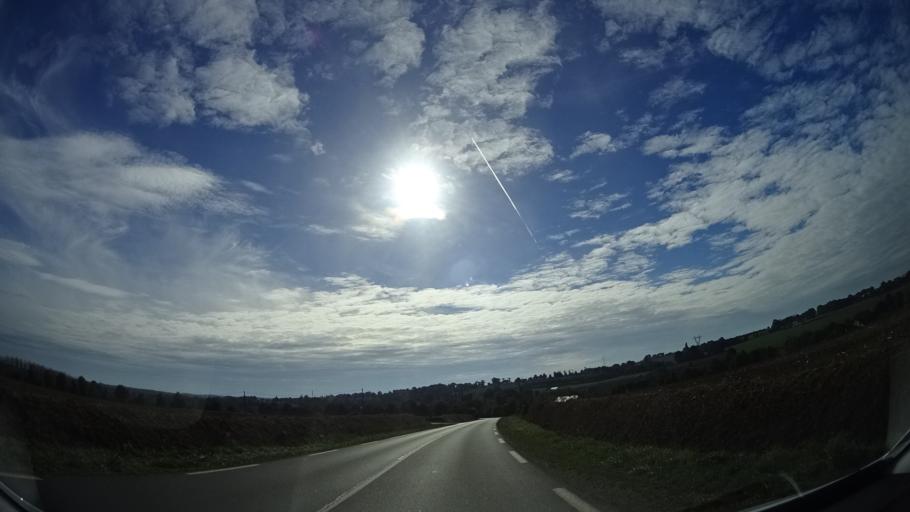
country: FR
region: Brittany
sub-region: Departement d'Ille-et-Vilaine
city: Geveze
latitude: 48.2379
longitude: -1.8063
